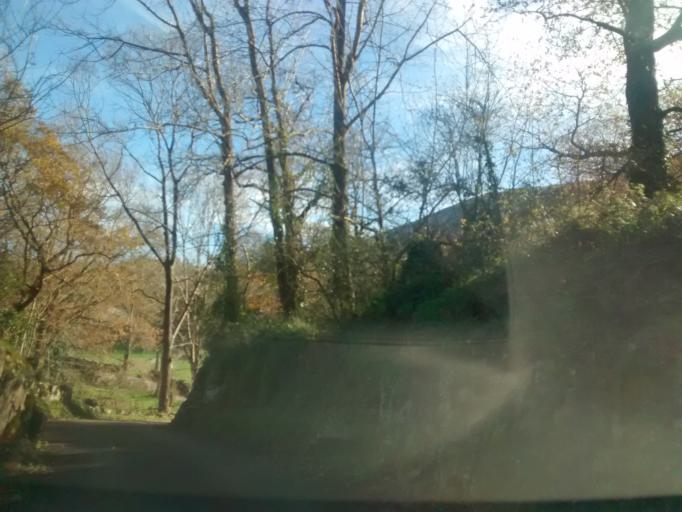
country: ES
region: Cantabria
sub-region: Provincia de Cantabria
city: Entrambasaguas
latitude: 43.3418
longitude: -3.6948
